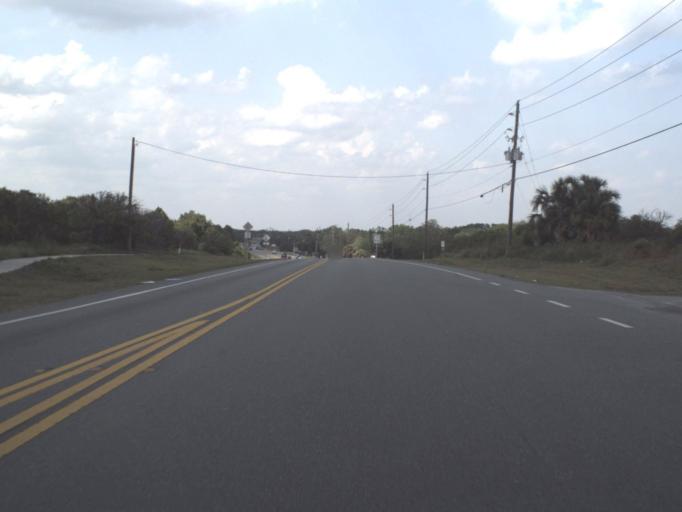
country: US
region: Florida
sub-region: Lake County
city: Tavares
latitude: 28.7736
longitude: -81.7488
